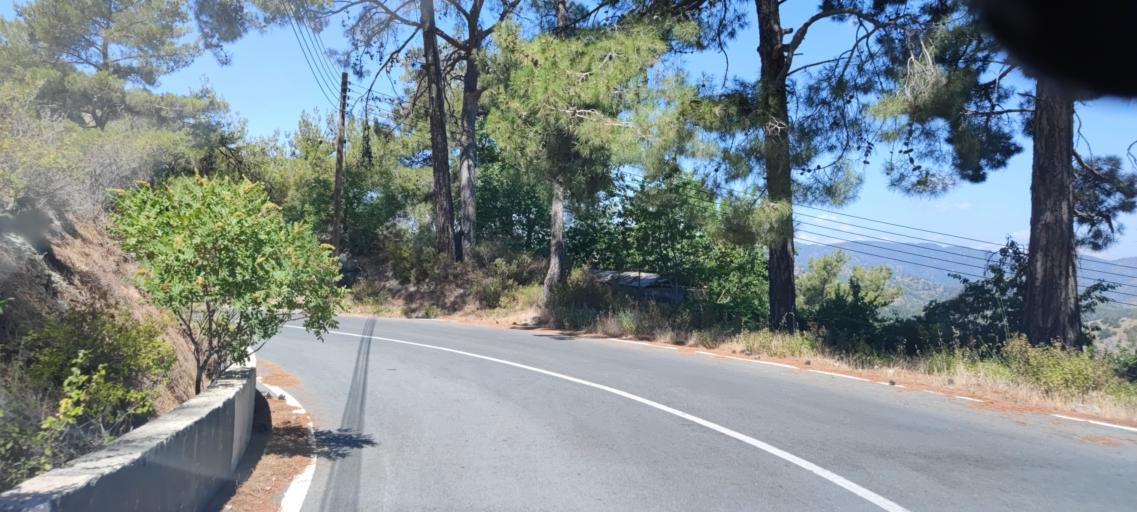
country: CY
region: Lefkosia
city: Kakopetria
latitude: 34.9198
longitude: 32.8131
